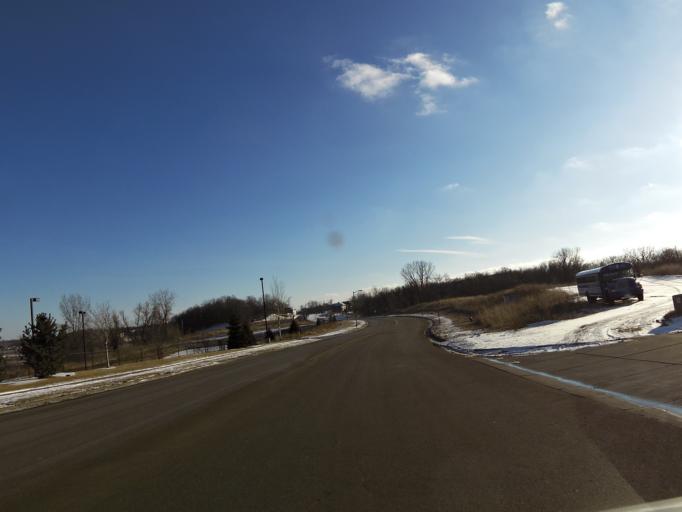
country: US
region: Minnesota
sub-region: Scott County
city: Prior Lake
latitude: 44.7496
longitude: -93.4498
